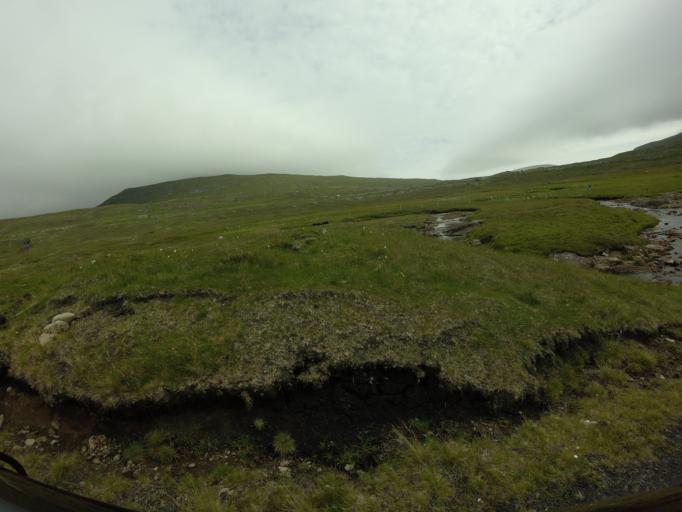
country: FO
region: Sandoy
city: Sandur
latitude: 61.8202
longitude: -6.7501
